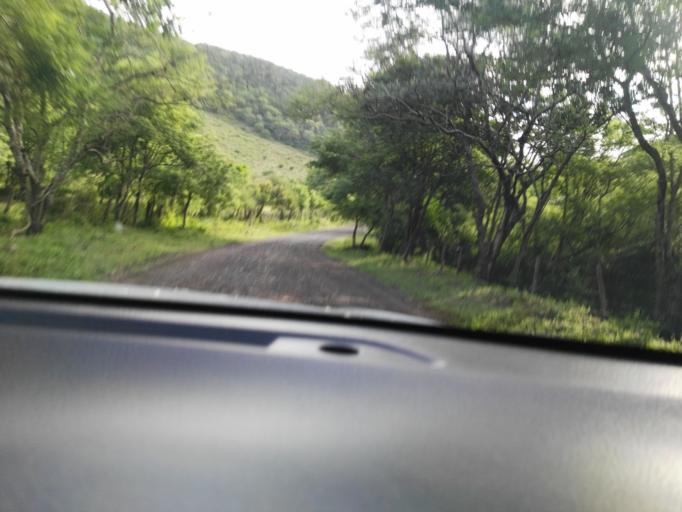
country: NI
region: Matagalpa
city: Terrabona
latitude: 12.8485
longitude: -86.0420
